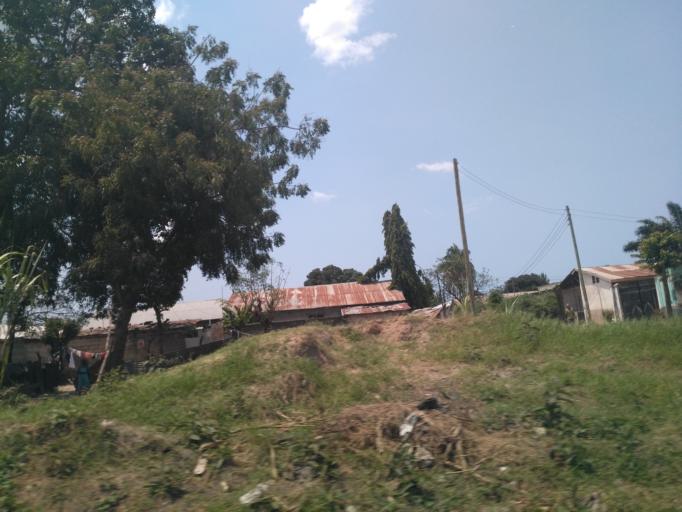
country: TZ
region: Dar es Salaam
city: Dar es Salaam
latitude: -6.8262
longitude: 39.3087
